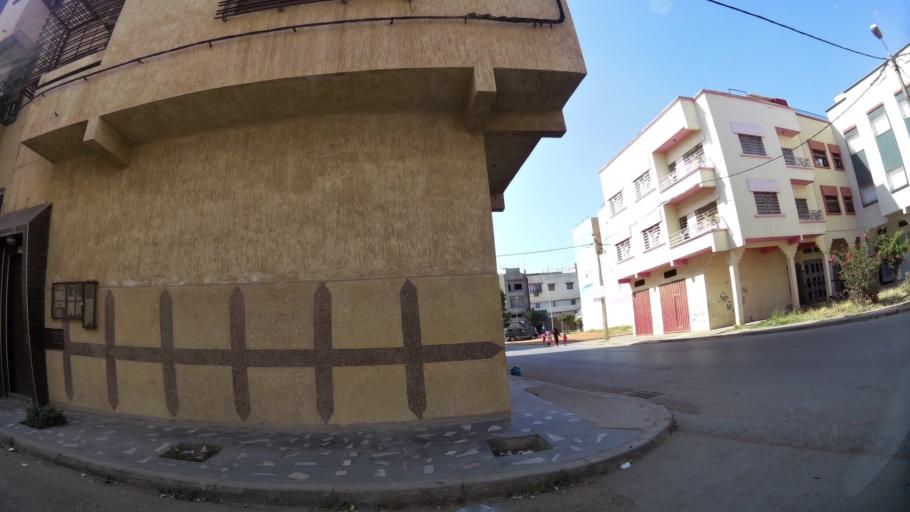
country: MA
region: Rabat-Sale-Zemmour-Zaer
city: Sale
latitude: 34.0656
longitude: -6.7637
